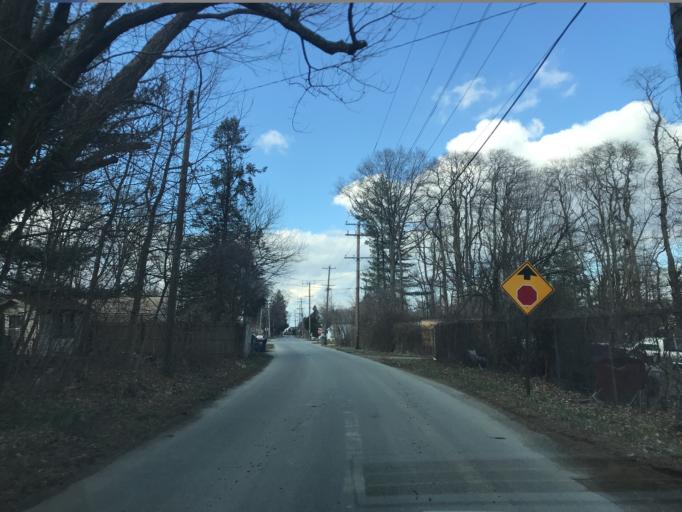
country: US
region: Pennsylvania
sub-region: Chester County
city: Oxford
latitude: 39.7526
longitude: -76.0147
